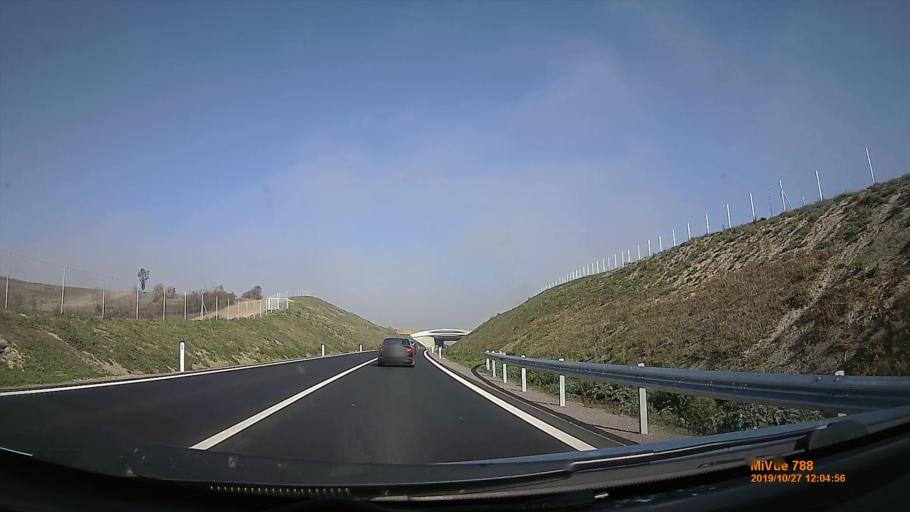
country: AT
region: Lower Austria
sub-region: Politischer Bezirk Mistelbach
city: Drasenhofen
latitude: 48.7581
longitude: 16.6345
